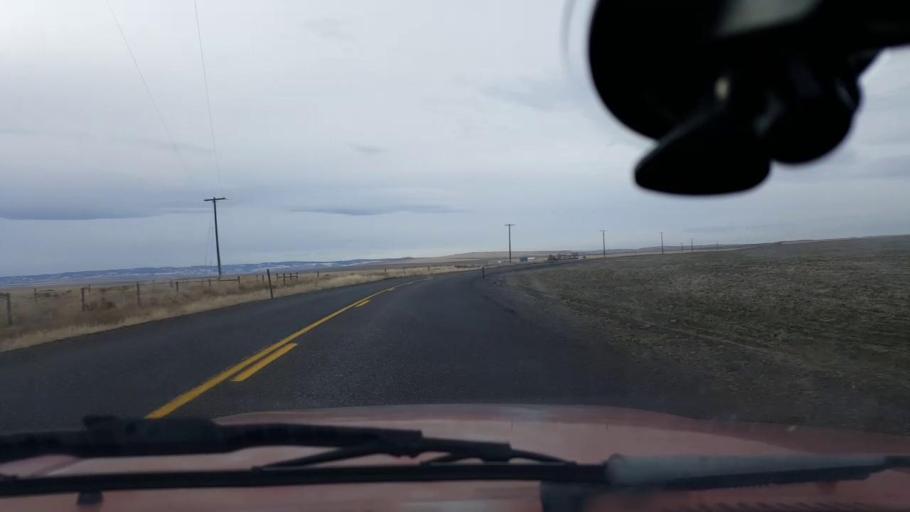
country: US
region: Washington
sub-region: Asotin County
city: Clarkston Heights-Vineland
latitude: 46.3753
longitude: -117.1571
